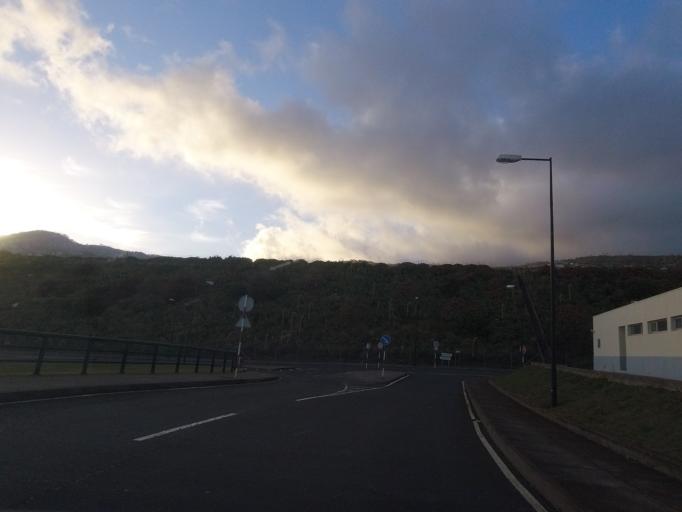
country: PT
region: Madeira
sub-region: Machico
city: Machico
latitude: 32.6903
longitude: -16.7813
